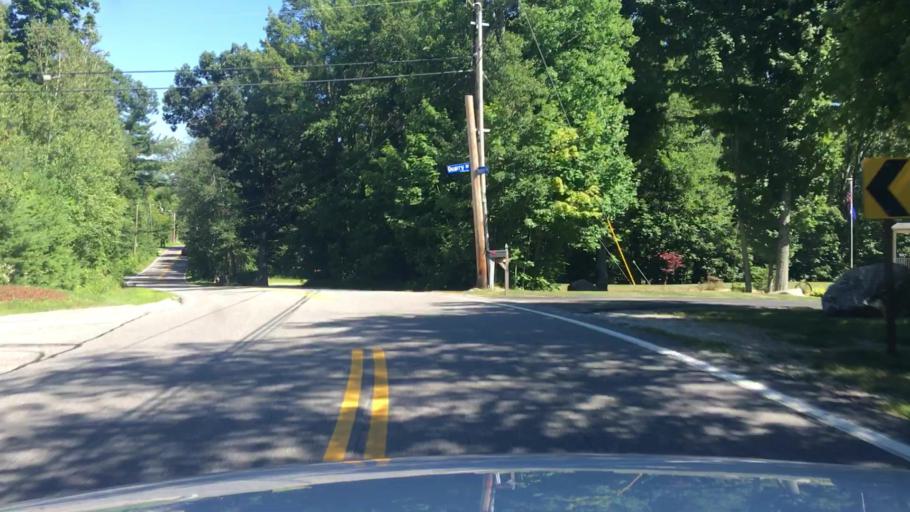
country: US
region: New Hampshire
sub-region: Merrimack County
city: South Hooksett
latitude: 43.0384
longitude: -71.4048
